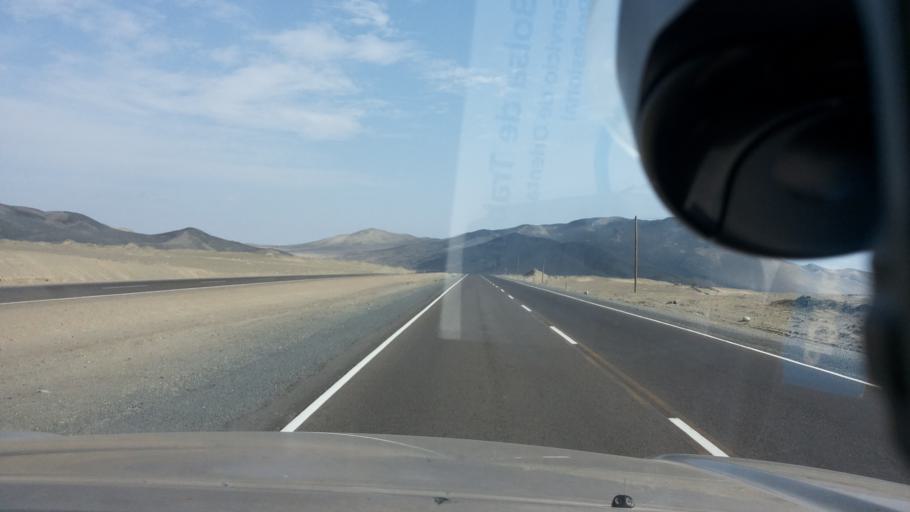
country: PE
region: Ancash
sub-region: Provincia de Huarmey
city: La Caleta Culebras
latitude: -9.7191
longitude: -78.2707
